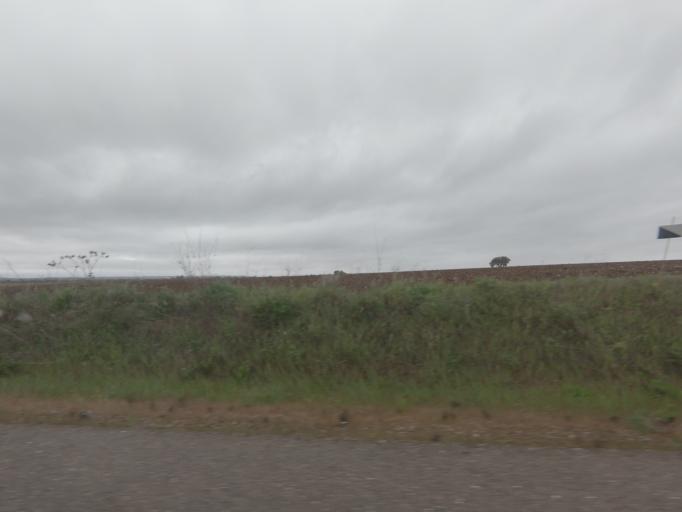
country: ES
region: Extremadura
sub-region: Provincia de Badajoz
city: Villar del Rey
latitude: 39.0512
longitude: -6.7994
